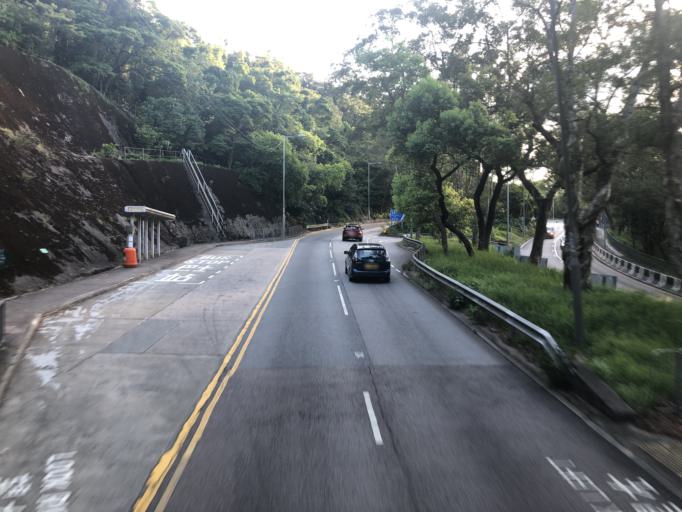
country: HK
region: Sai Kung
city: Sai Kung
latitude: 22.3433
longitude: 114.2519
